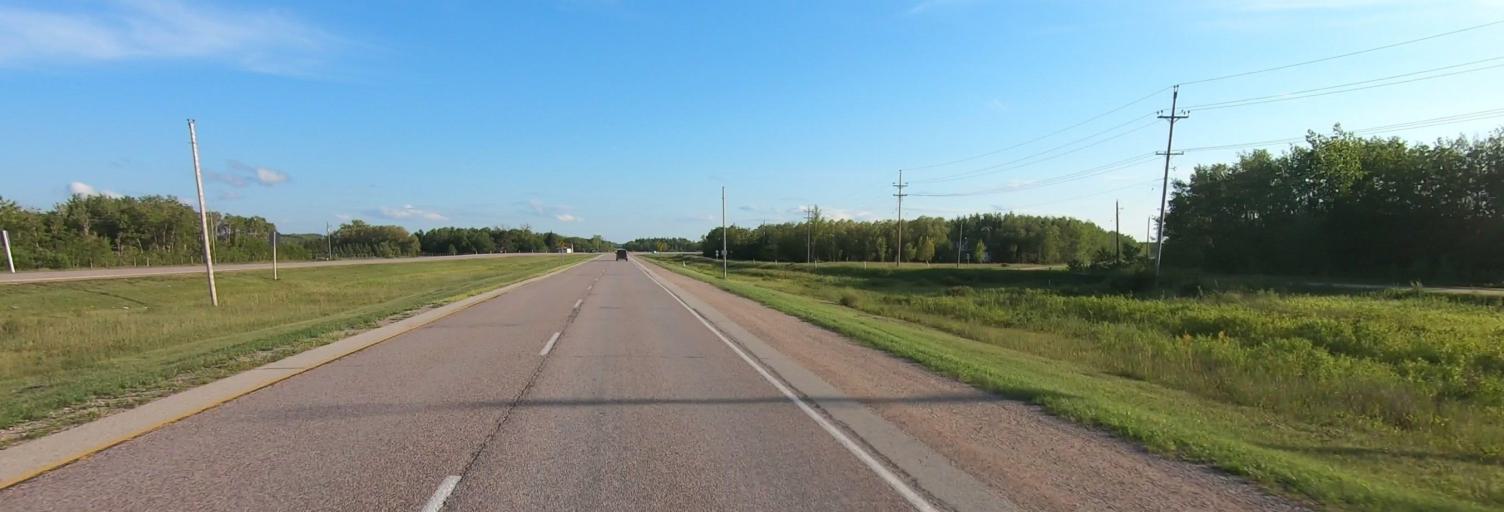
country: CA
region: Manitoba
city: Selkirk
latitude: 50.0924
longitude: -96.8642
